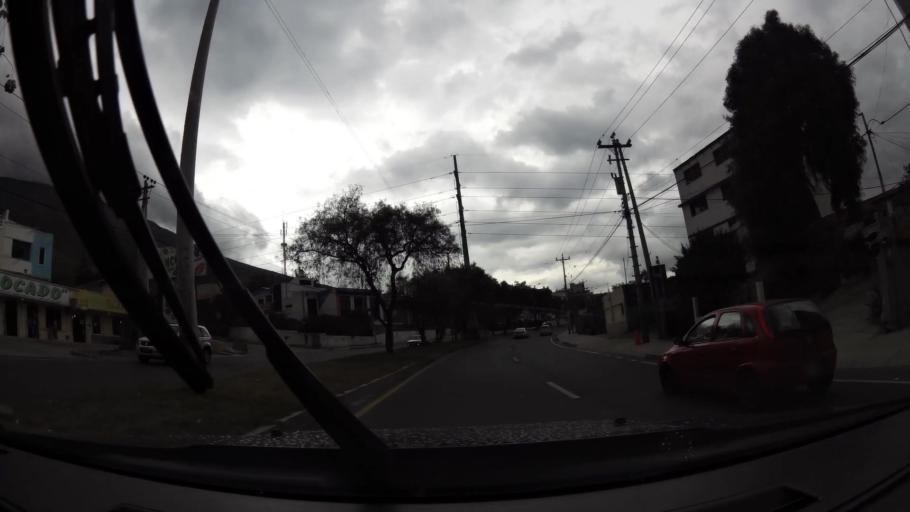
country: EC
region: Pichincha
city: Quito
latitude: -0.0507
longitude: -78.4566
